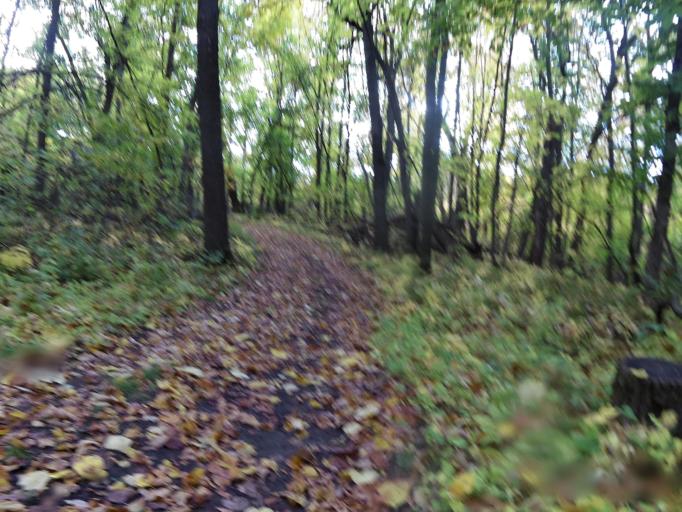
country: US
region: North Dakota
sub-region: Pembina County
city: Cavalier
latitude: 48.7781
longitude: -97.7332
